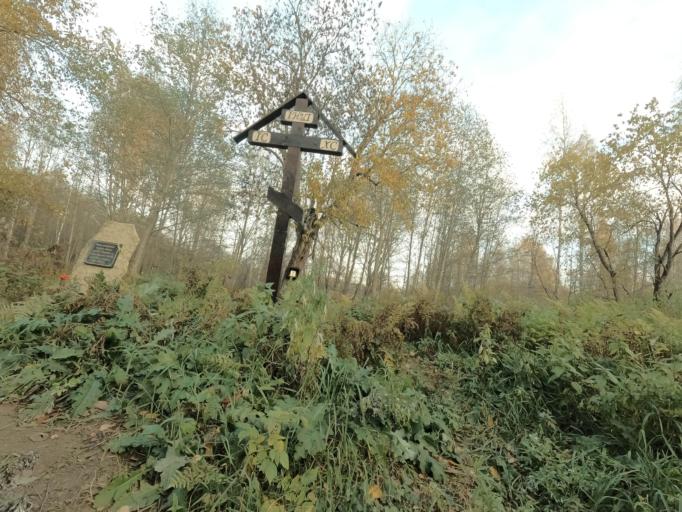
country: RU
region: Leningrad
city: Priladozhskiy
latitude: 59.7478
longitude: 31.3075
